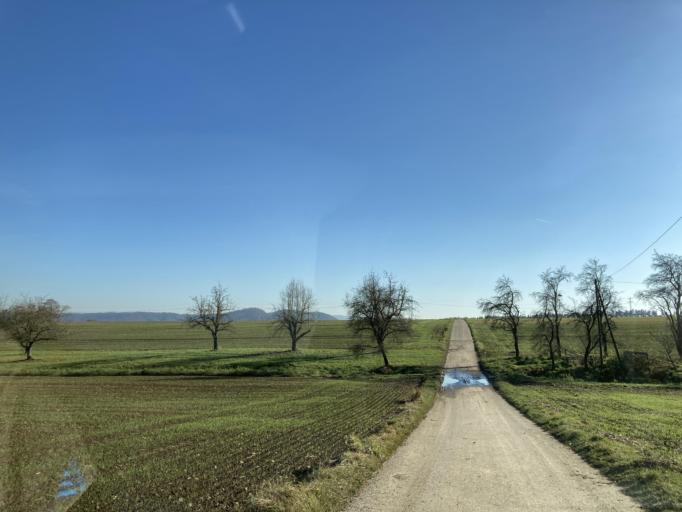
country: DE
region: Baden-Wuerttemberg
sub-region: Tuebingen Region
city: Rottenburg
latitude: 48.4739
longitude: 8.8900
